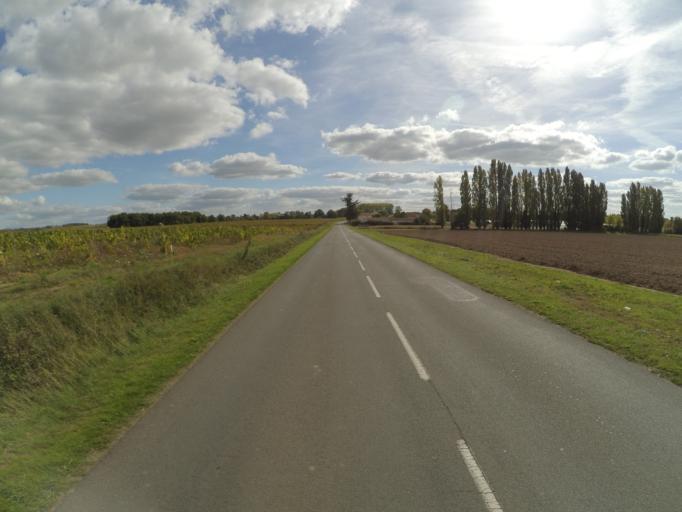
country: FR
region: Pays de la Loire
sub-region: Departement de la Loire-Atlantique
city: Le Loroux-Bottereau
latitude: 47.2081
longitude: -1.3498
